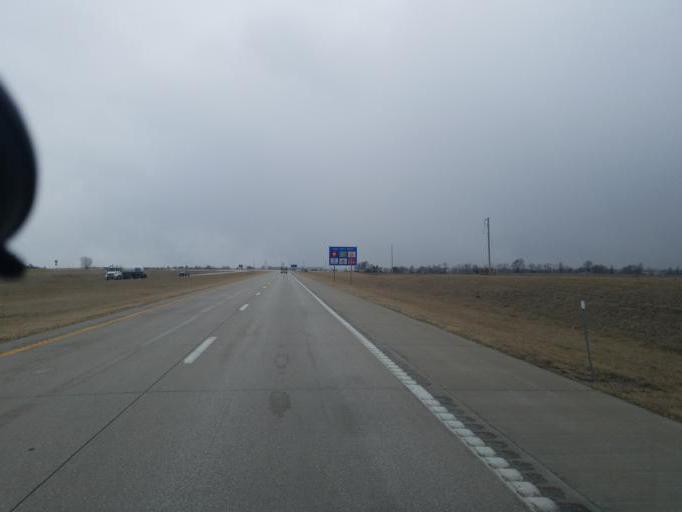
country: US
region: Missouri
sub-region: Randolph County
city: Moberly
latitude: 39.4652
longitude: -92.4352
